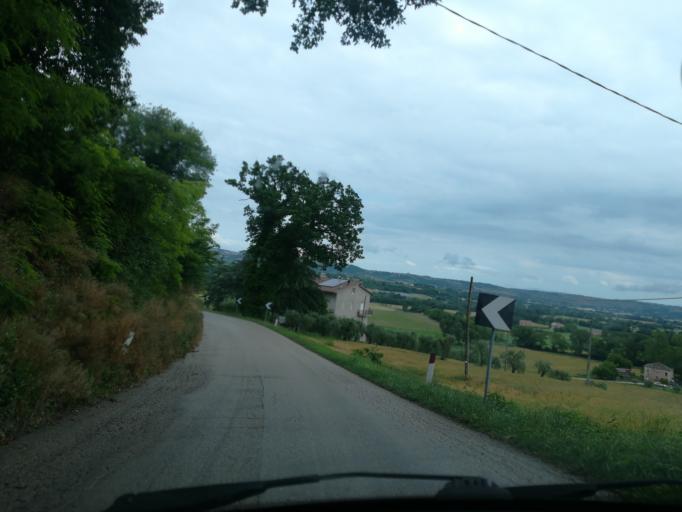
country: IT
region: The Marches
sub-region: Provincia di Macerata
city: Petriolo
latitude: 43.2268
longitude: 13.4641
